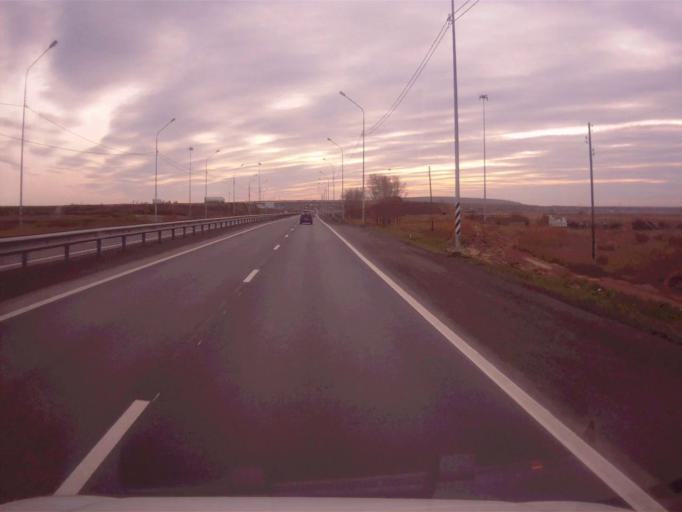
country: RU
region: Chelyabinsk
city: Roza
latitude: 54.9998
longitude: 61.4524
